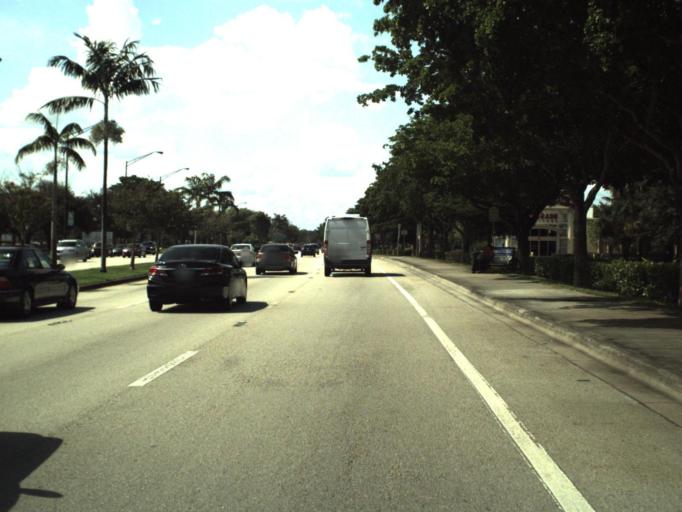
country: US
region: Florida
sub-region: Broward County
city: Plantation
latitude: 26.1154
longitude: -80.2506
